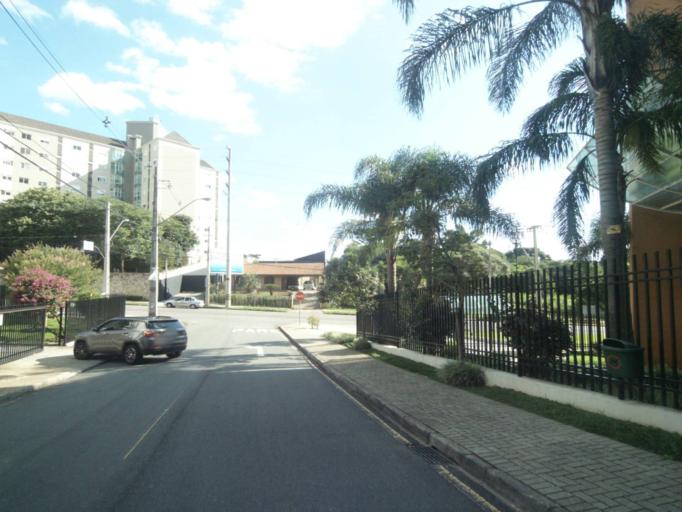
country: BR
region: Parana
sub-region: Curitiba
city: Curitiba
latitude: -25.4384
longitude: -49.3247
